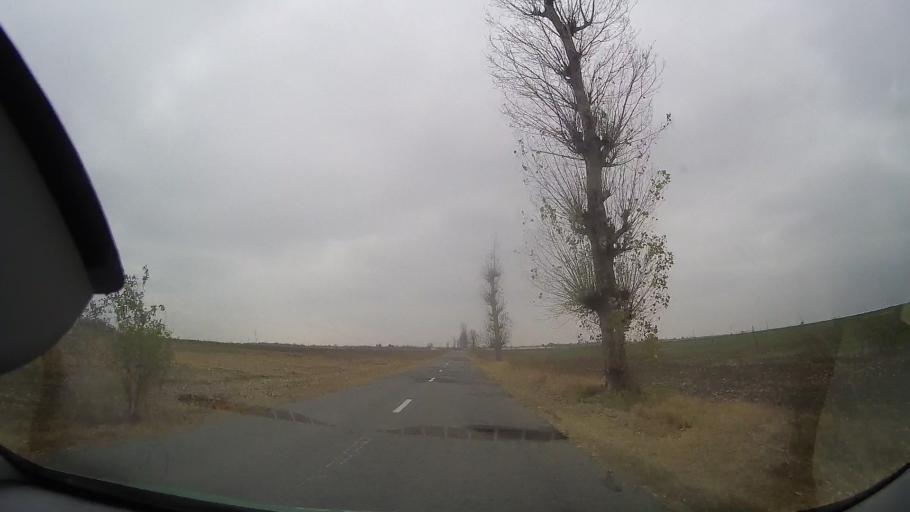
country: RO
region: Ialomita
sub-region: Comuna Valea Macrisului
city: Valea Macrisului
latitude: 44.7351
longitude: 26.8524
